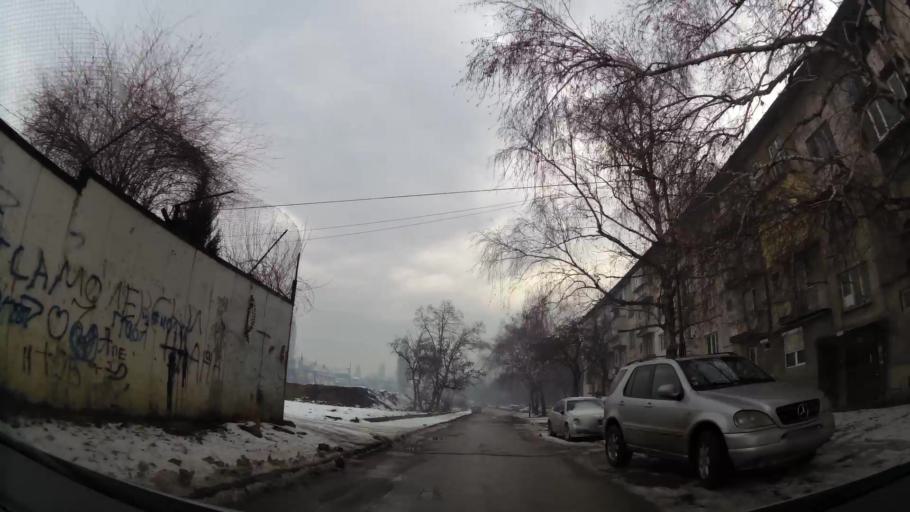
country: BG
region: Sofia-Capital
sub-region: Stolichna Obshtina
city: Sofia
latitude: 42.6929
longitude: 23.2770
